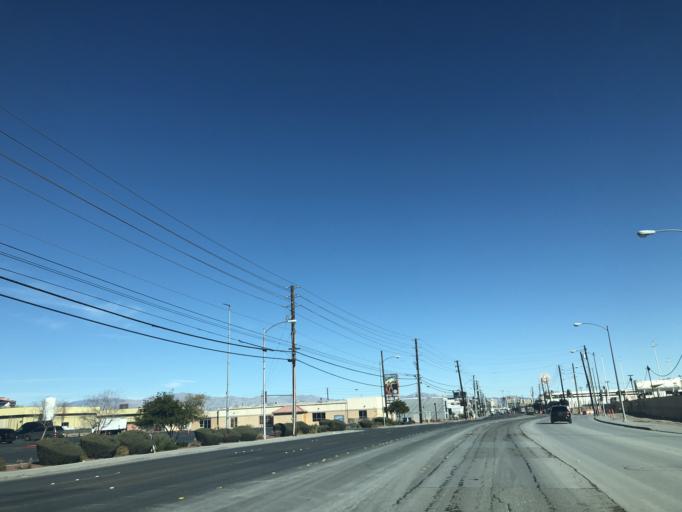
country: US
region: Nevada
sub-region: Clark County
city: Paradise
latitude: 36.1358
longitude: -115.1703
